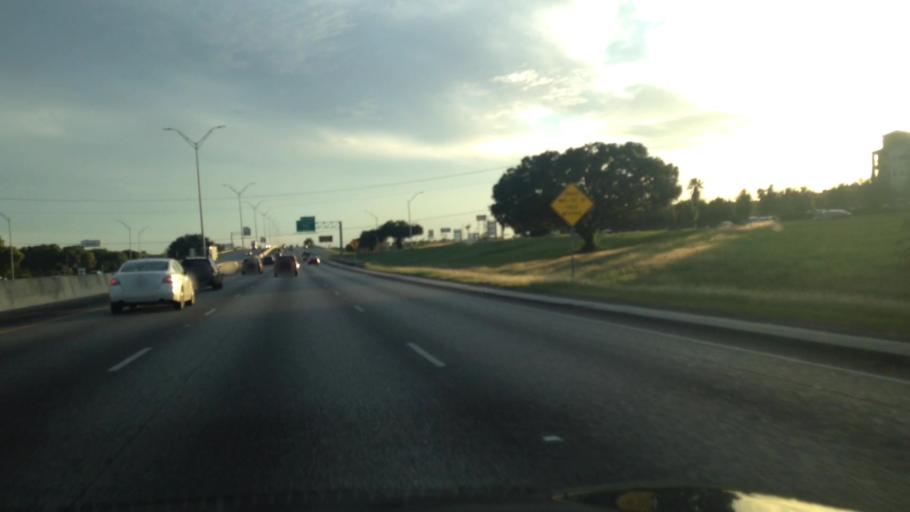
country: US
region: Texas
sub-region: Hays County
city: San Marcos
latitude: 29.8896
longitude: -97.9162
